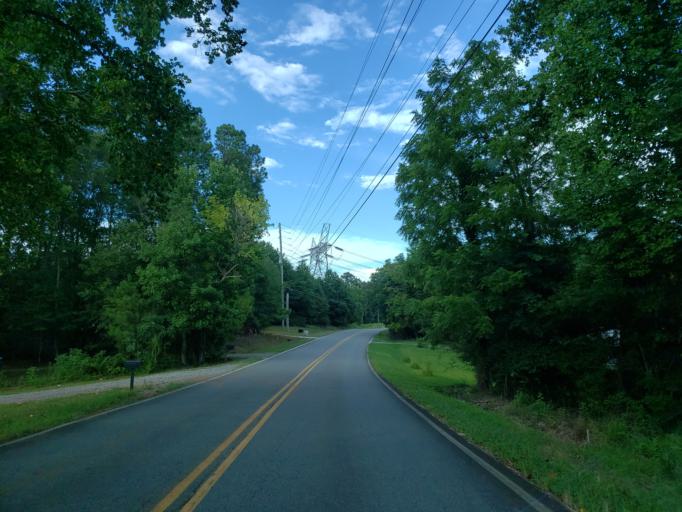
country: US
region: Georgia
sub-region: Cherokee County
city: Canton
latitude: 34.3248
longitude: -84.5157
